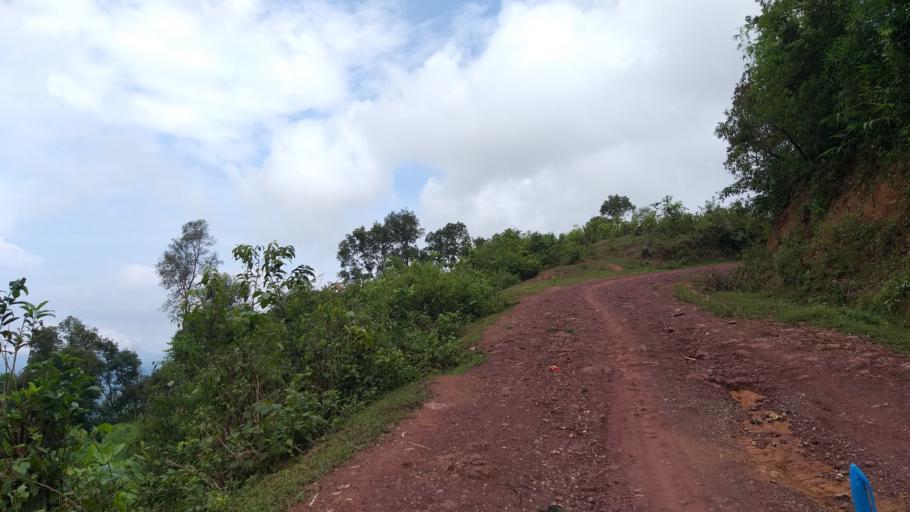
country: LA
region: Phongsali
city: Khoa
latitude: 21.3797
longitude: 102.6337
